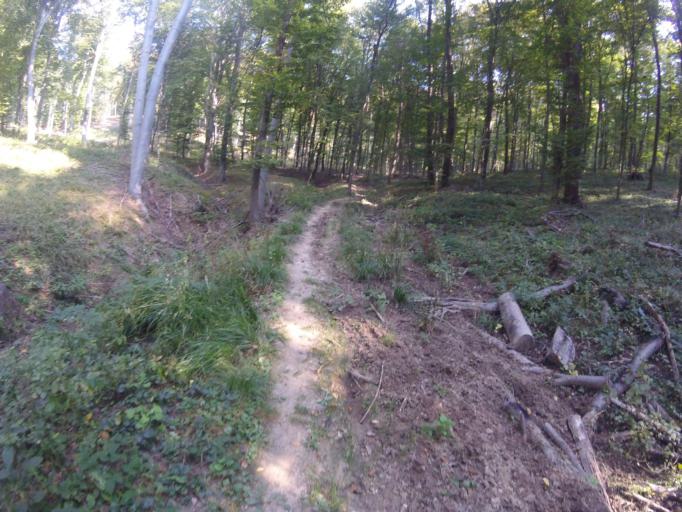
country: HU
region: Komarom-Esztergom
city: Piliscsev
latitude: 47.7133
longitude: 18.8451
